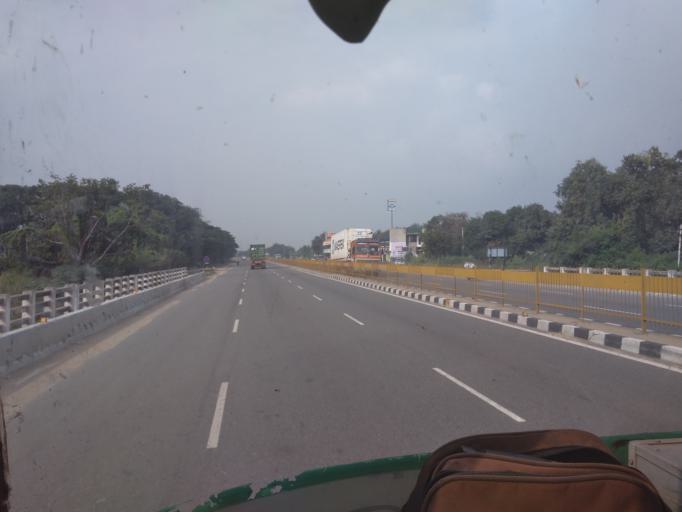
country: IN
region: Tamil Nadu
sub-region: Vellore
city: Pallikondai
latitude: 12.9022
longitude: 78.9356
